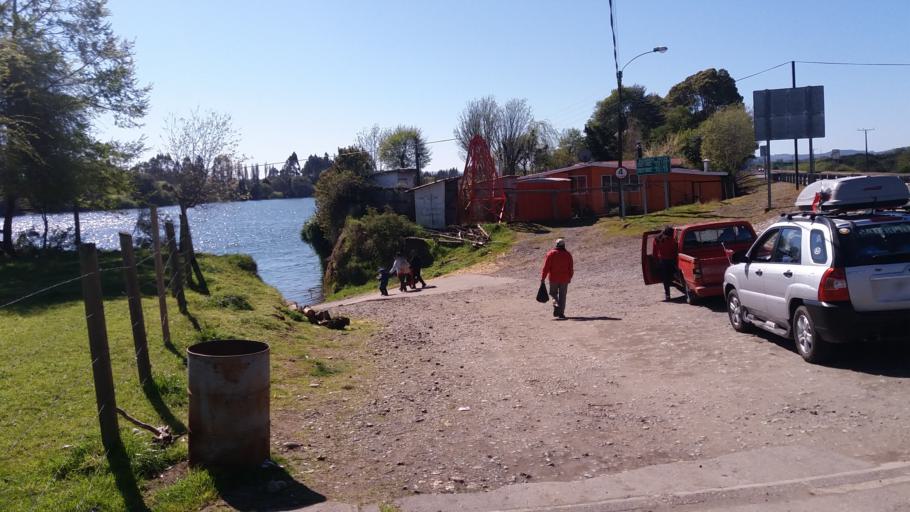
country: CL
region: Araucania
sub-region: Provincia de Cautin
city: Carahue
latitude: -39.1740
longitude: -73.1712
